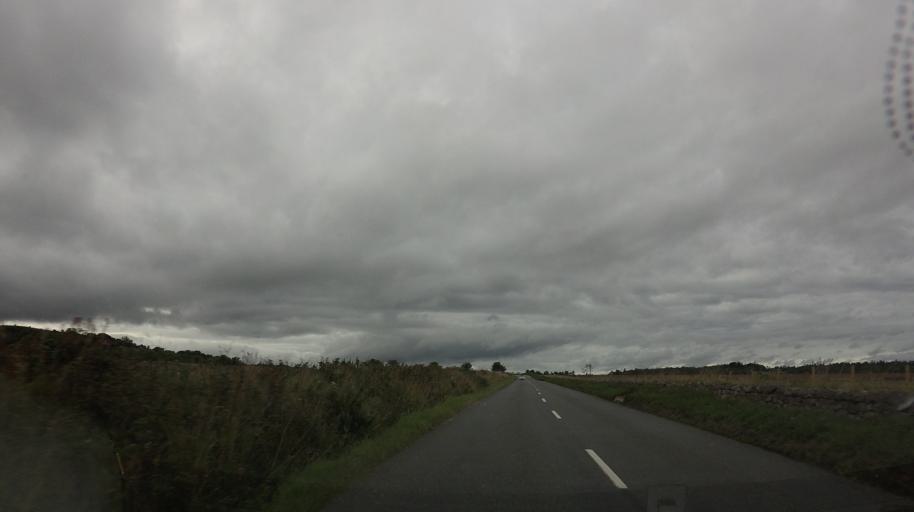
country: GB
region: Scotland
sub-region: Aberdeenshire
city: Kemnay
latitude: 57.1458
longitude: -2.4349
